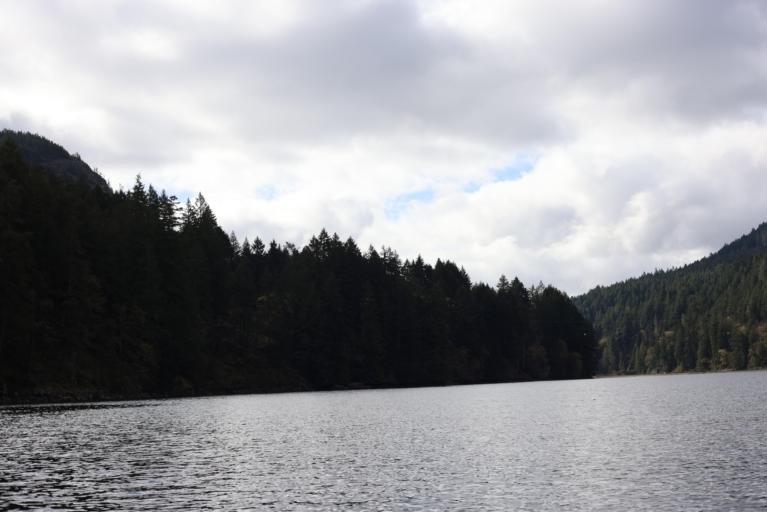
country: CA
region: British Columbia
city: Langford
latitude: 48.4978
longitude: -123.5495
